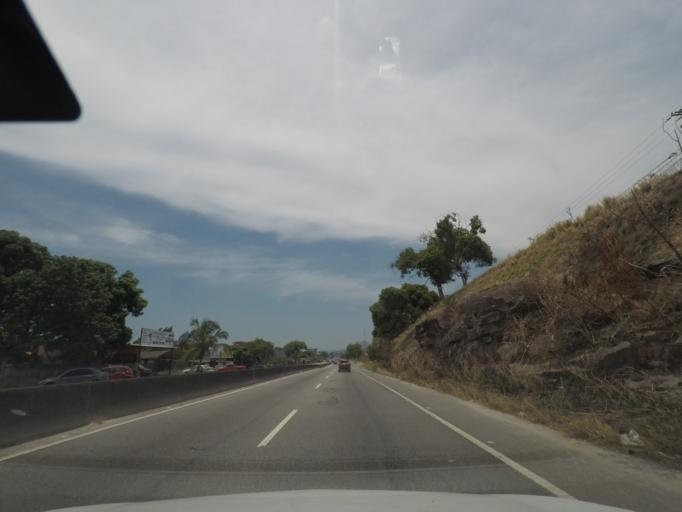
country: BR
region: Rio de Janeiro
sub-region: Marica
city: Marica
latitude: -22.9315
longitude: -42.8811
